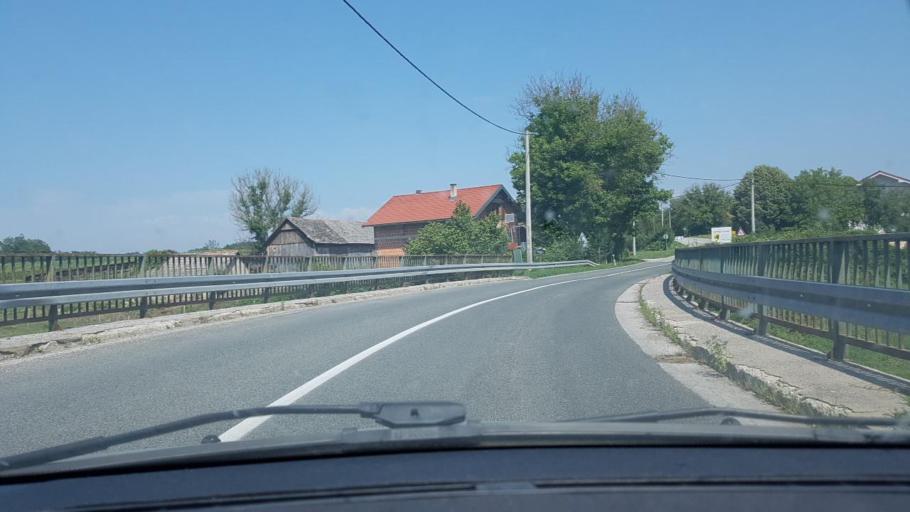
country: BA
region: Federation of Bosnia and Herzegovina
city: Velika Kladusa
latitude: 45.2099
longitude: 15.7701
